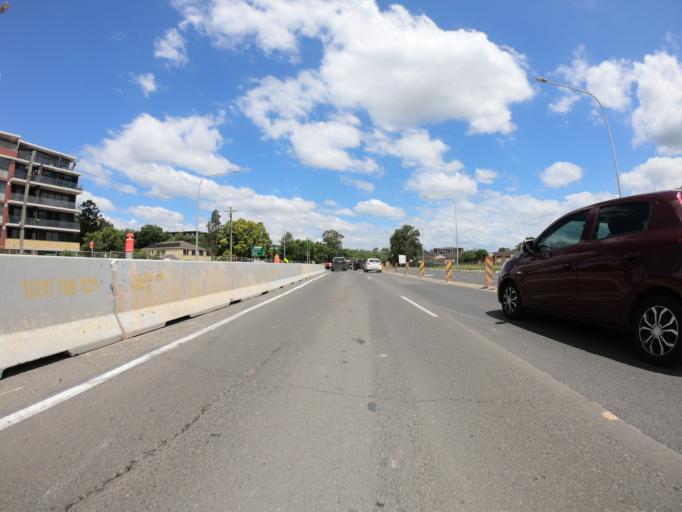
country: AU
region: New South Wales
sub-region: Penrith Municipality
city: Penrith
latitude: -33.7527
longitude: 150.6874
